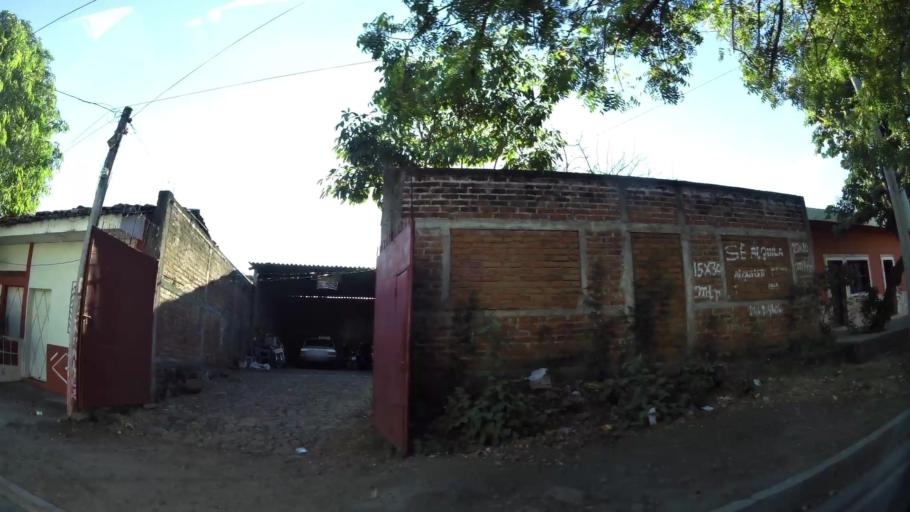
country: SV
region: San Miguel
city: San Miguel
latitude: 13.4870
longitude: -88.1670
